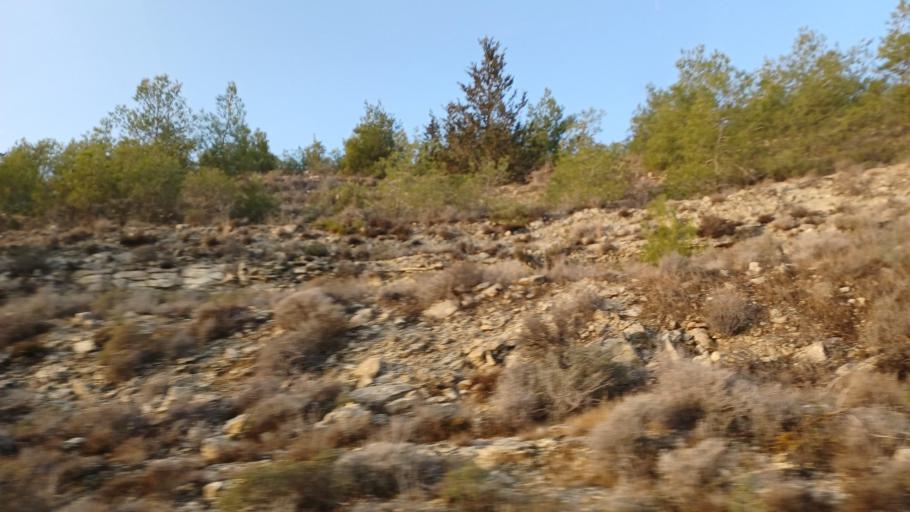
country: CY
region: Lefkosia
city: Lympia
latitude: 34.9972
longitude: 33.5243
